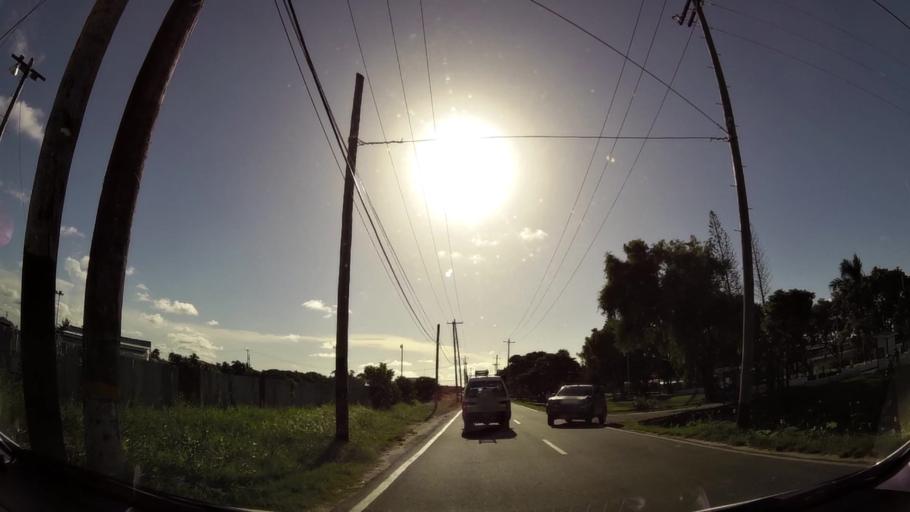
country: GY
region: Demerara-Mahaica
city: Georgetown
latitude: 6.8195
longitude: -58.1495
